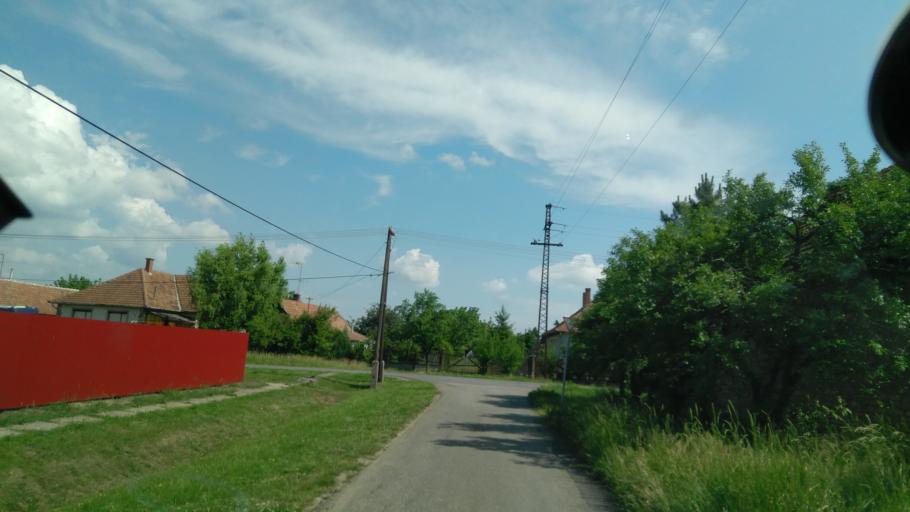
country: HU
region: Bekes
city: Doboz
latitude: 46.7390
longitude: 21.2344
